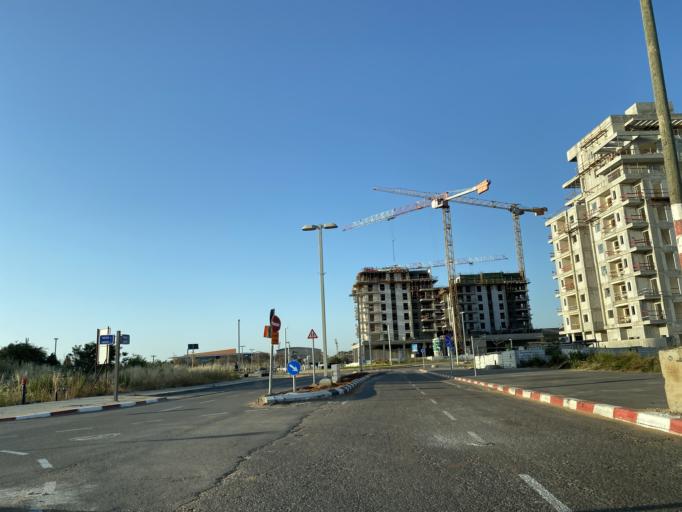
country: IL
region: Tel Aviv
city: Herzliyya
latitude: 32.1604
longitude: 34.8236
